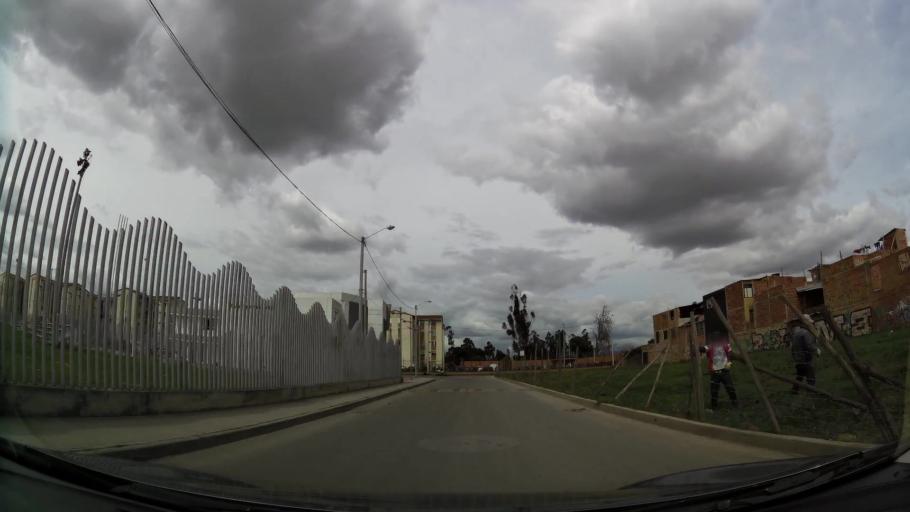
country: CO
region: Cundinamarca
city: Funza
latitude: 4.7107
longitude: -74.1969
